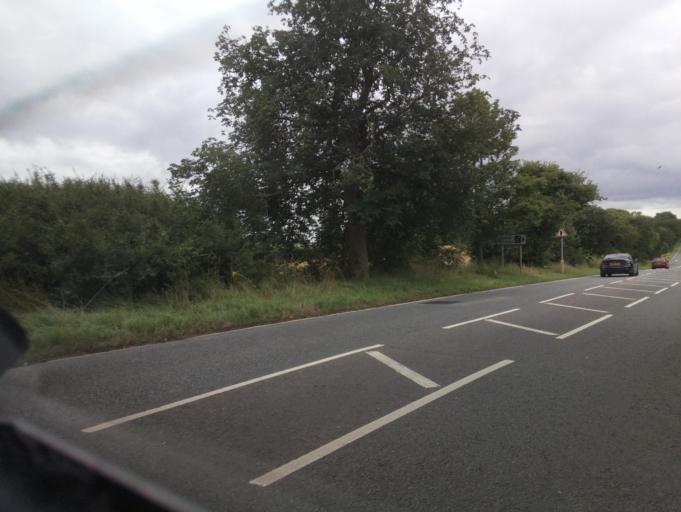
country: GB
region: England
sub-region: District of Rutland
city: Ryhall
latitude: 52.6675
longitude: -0.4682
